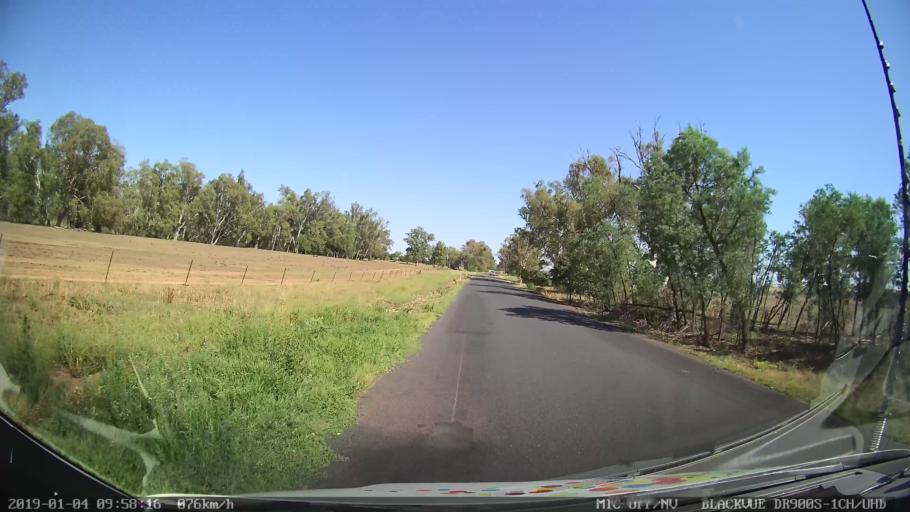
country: AU
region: New South Wales
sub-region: Cabonne
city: Canowindra
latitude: -33.5200
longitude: 148.3956
